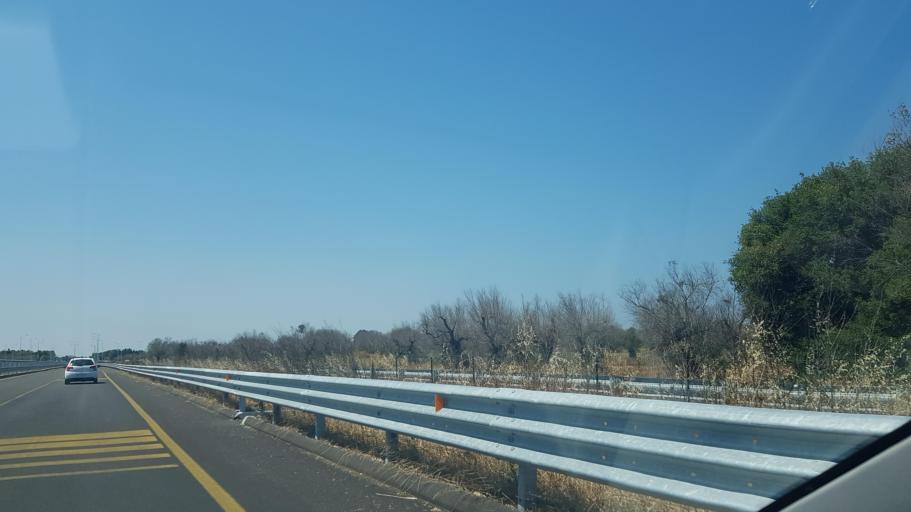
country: IT
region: Apulia
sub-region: Provincia di Lecce
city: Struda
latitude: 40.3228
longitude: 18.2636
